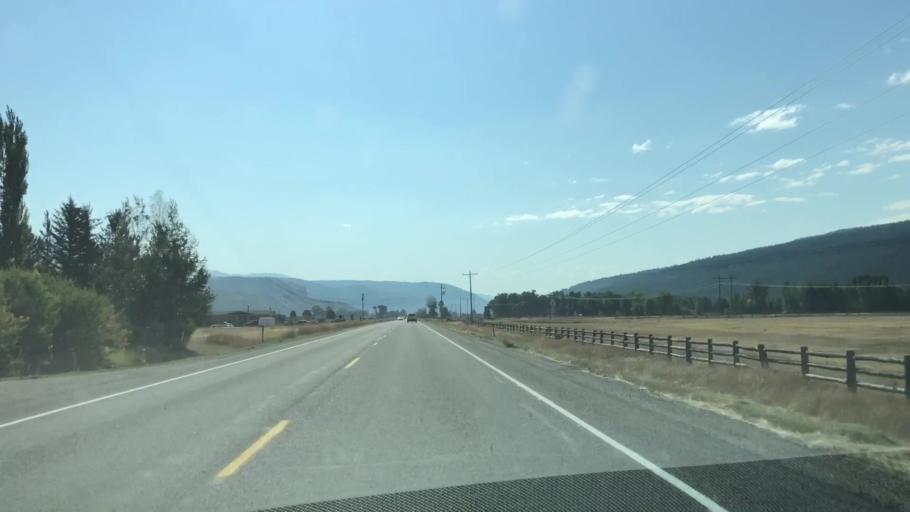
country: US
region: Idaho
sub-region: Teton County
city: Victor
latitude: 43.3980
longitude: -111.2825
